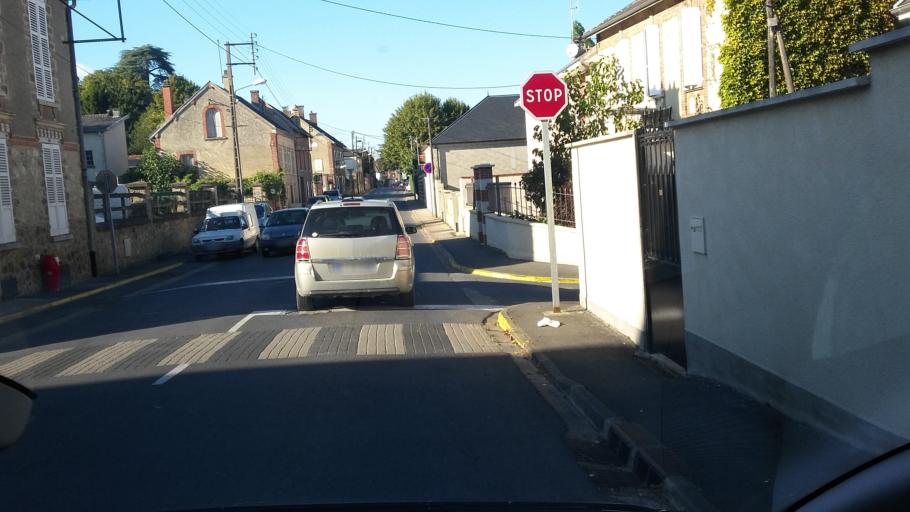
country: FR
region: Champagne-Ardenne
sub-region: Departement de la Marne
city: Avize
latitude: 48.9678
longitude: 4.0081
